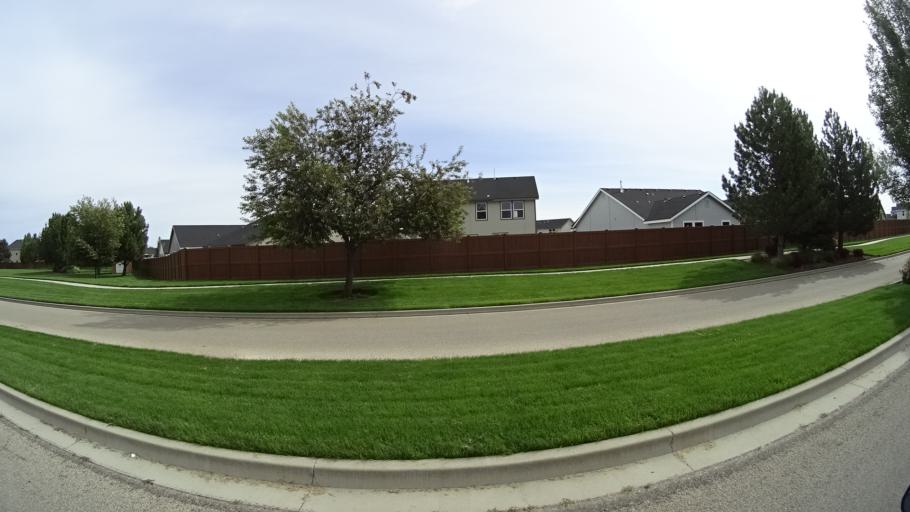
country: US
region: Idaho
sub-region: Ada County
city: Garden City
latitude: 43.5338
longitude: -116.2997
